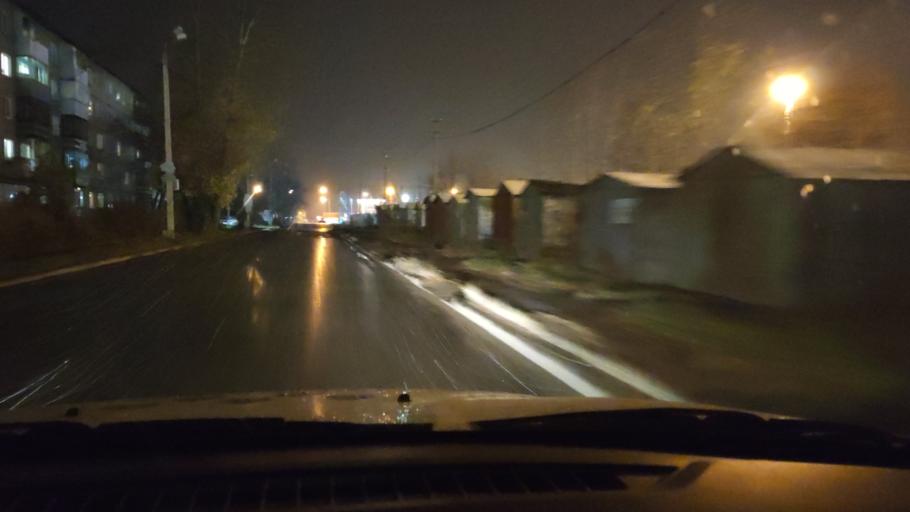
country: RU
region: Perm
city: Kondratovo
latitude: 57.9514
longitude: 56.1169
